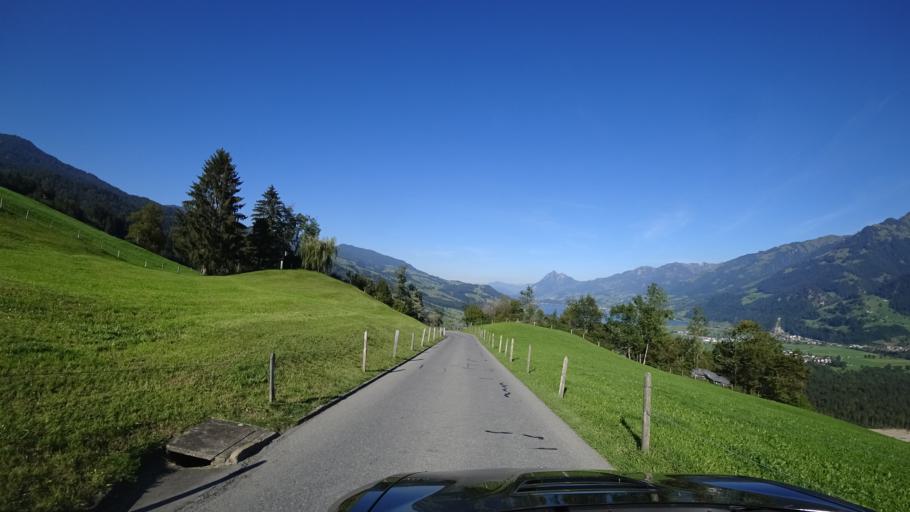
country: CH
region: Obwalden
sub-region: Obwalden
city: Giswil
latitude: 46.8375
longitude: 8.1450
